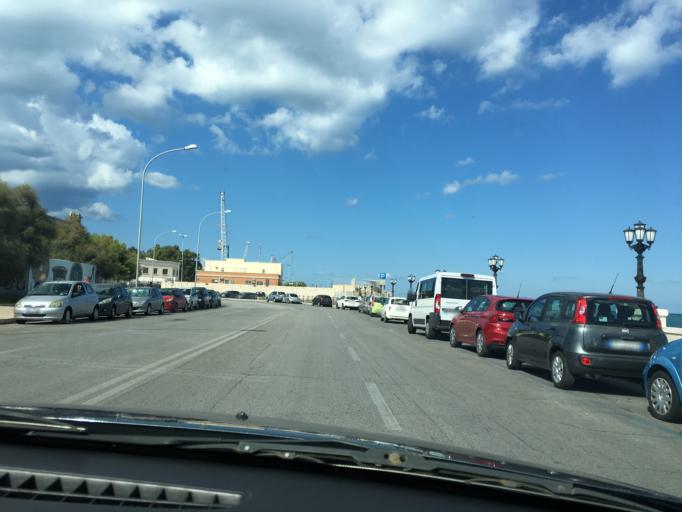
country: IT
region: Apulia
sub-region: Provincia di Bari
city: Bari
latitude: 41.1321
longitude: 16.8716
